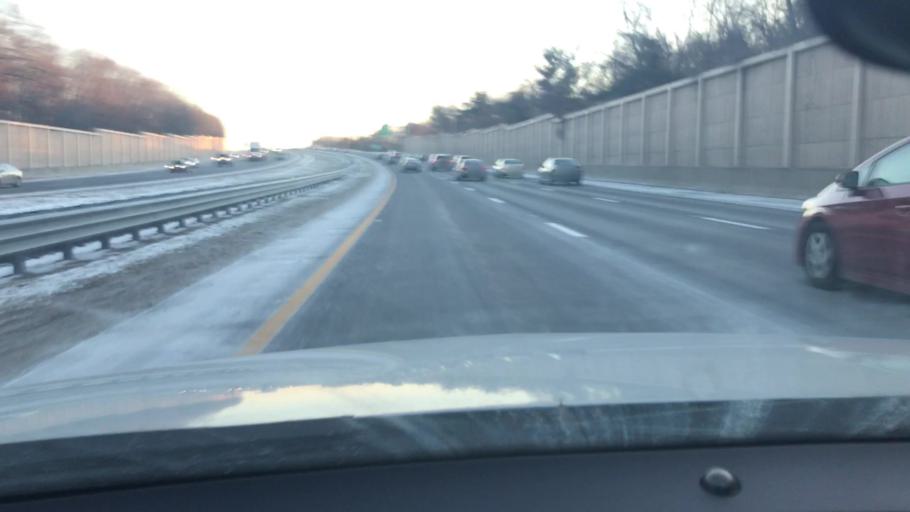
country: US
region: New Jersey
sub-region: Mercer County
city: Mercerville
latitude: 40.2386
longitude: -74.7019
